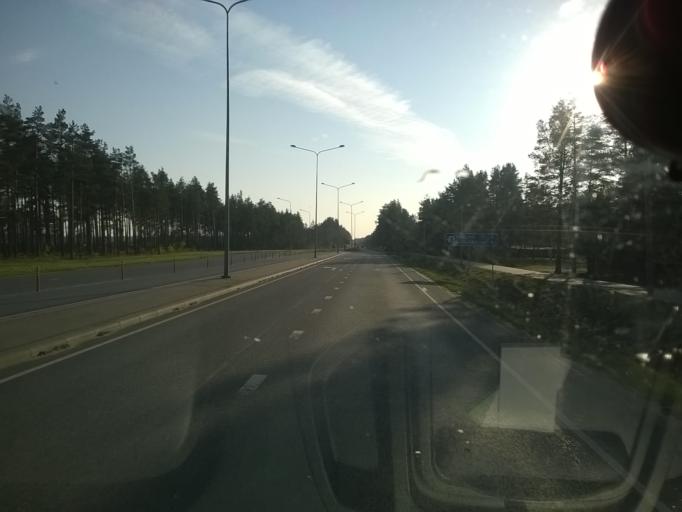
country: EE
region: Harju
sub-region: Saku vald
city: Saku
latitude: 59.3335
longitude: 24.6966
